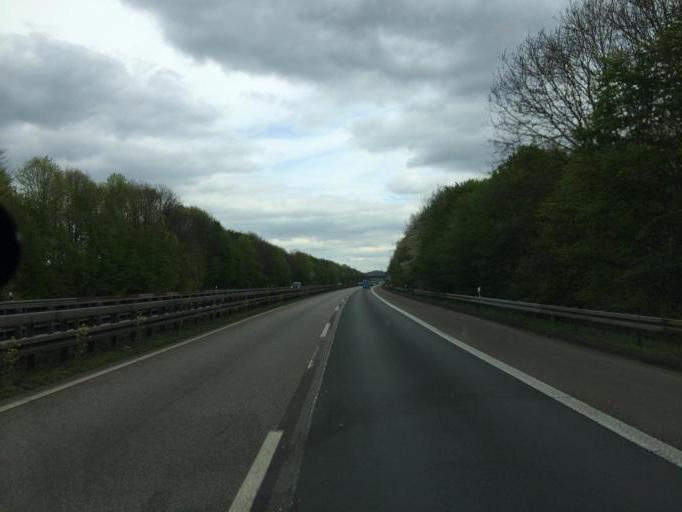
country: DE
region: North Rhine-Westphalia
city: Sprockhovel
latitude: 51.4195
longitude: 7.2662
